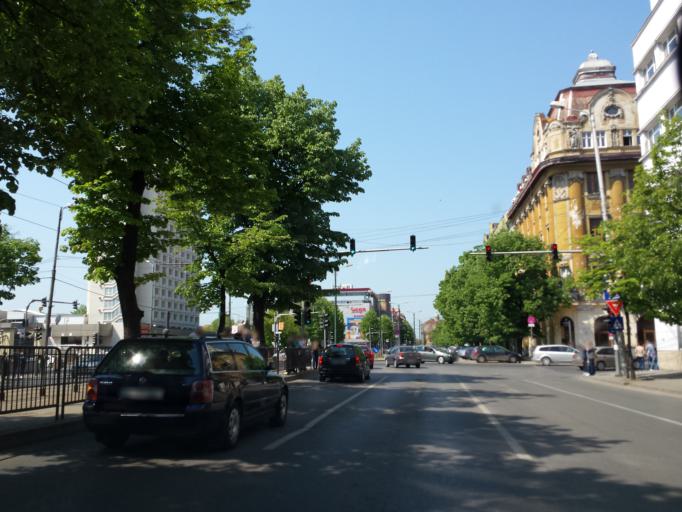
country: RO
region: Timis
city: Timisoara
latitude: 45.7557
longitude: 21.2343
